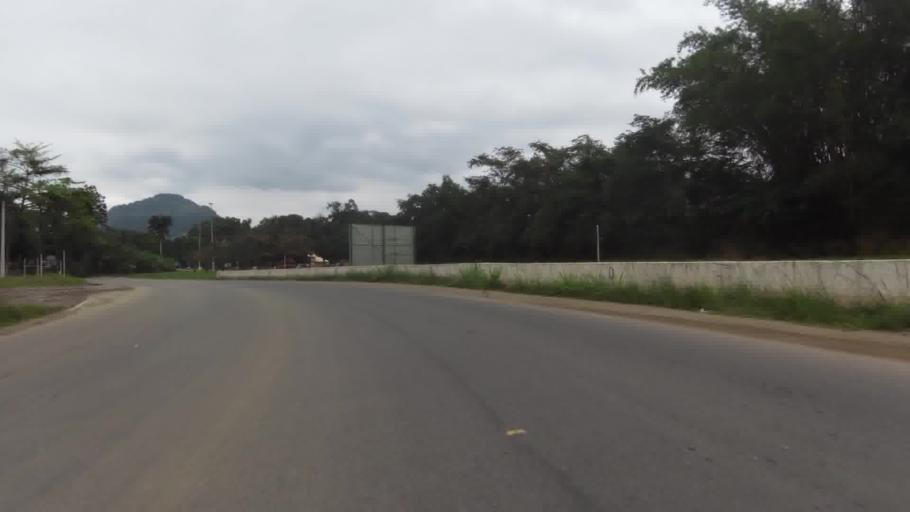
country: BR
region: Espirito Santo
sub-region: Iconha
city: Iconha
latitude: -20.7712
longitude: -40.7623
